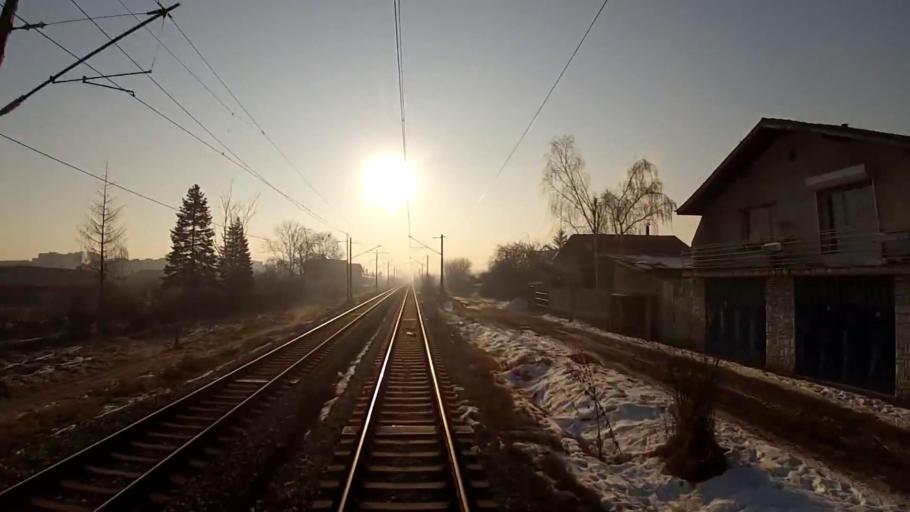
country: BG
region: Sofia-Capital
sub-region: Stolichna Obshtina
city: Sofia
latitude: 42.7342
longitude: 23.2688
